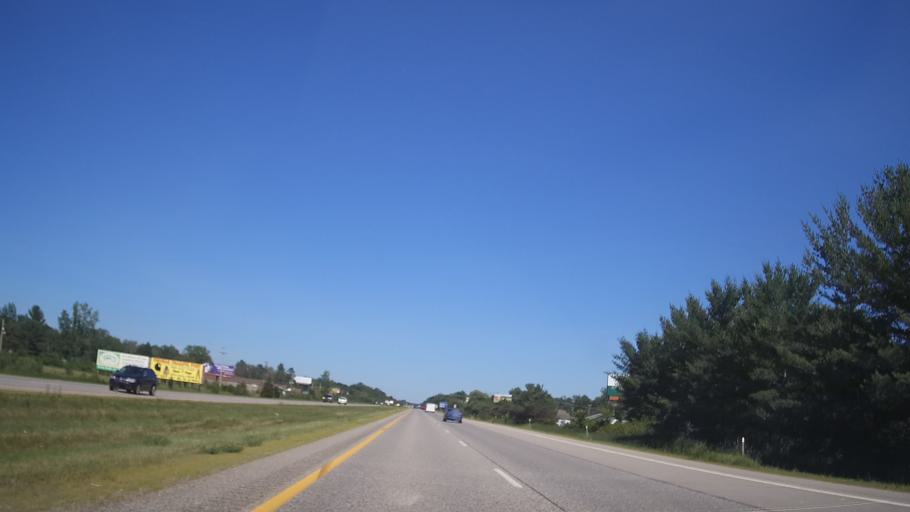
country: US
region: Michigan
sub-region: Midland County
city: Midland
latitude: 43.6562
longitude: -84.3028
